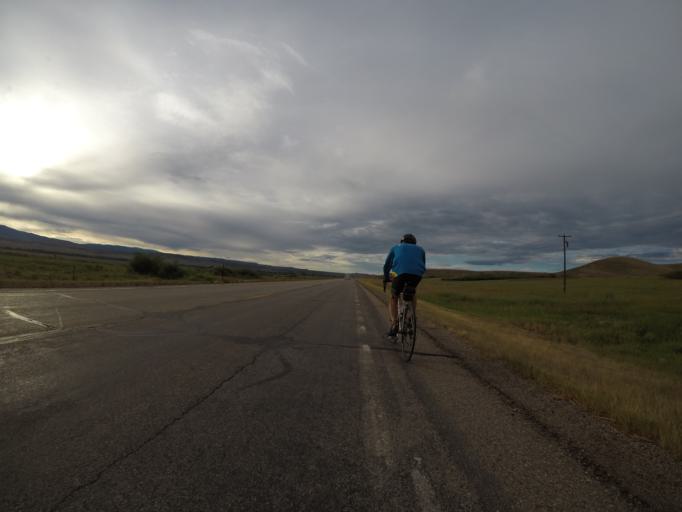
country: US
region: Wyoming
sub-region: Carbon County
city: Saratoga
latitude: 41.3937
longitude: -106.7617
